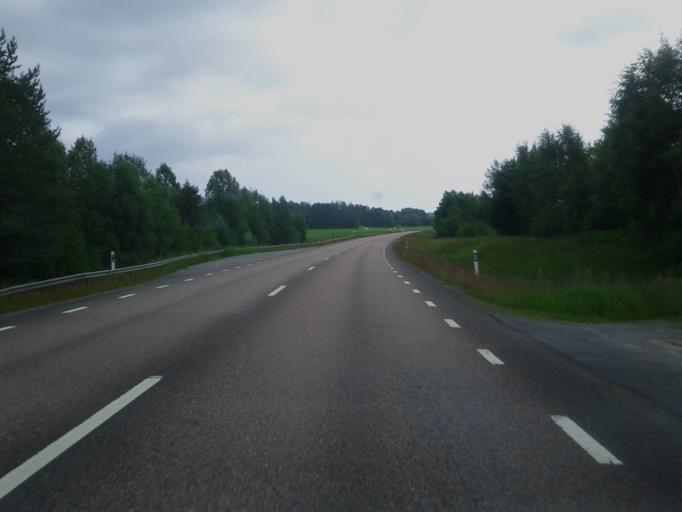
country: SE
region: Vaesterbotten
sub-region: Skelleftea Kommun
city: Burea
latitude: 64.3340
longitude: 21.2207
